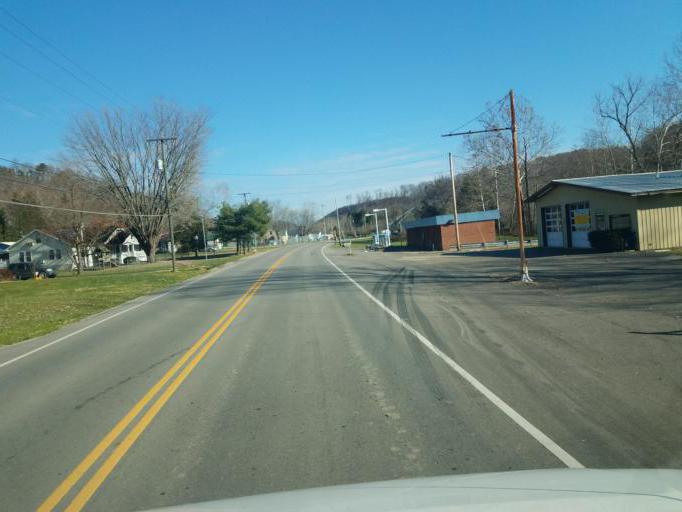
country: US
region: Ohio
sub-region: Scioto County
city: Sciotodale
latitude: 38.8509
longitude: -82.8938
